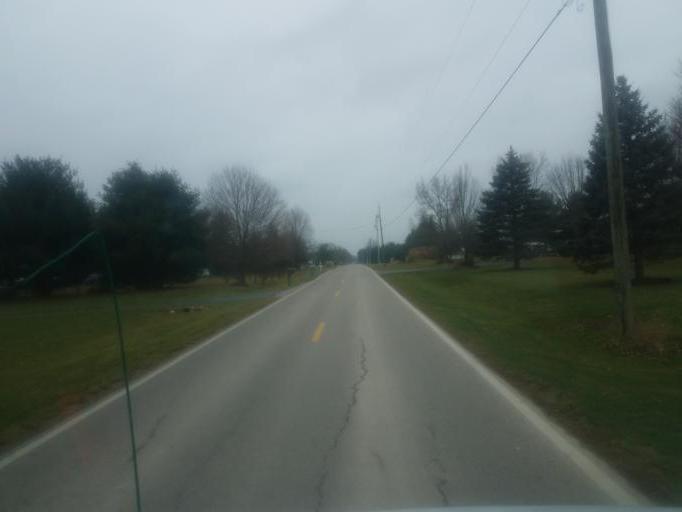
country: US
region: Ohio
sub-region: Delaware County
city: Sunbury
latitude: 40.2168
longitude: -82.9014
